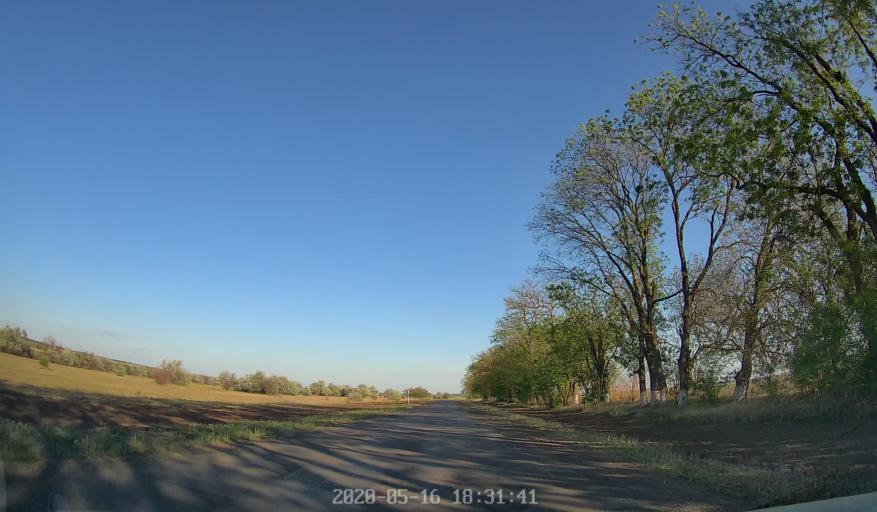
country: UA
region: Odessa
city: Lymanske
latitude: 46.5423
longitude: 30.0455
